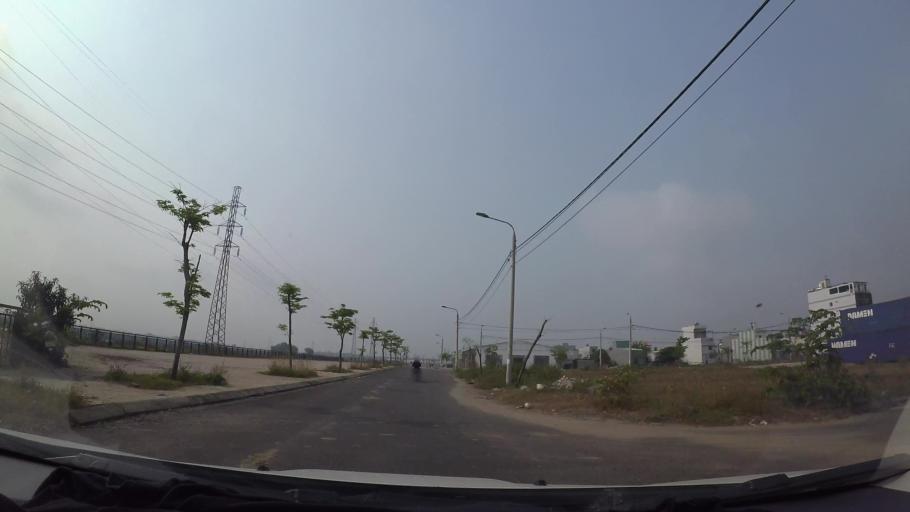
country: VN
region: Da Nang
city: Ngu Hanh Son
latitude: 16.0099
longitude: 108.2311
